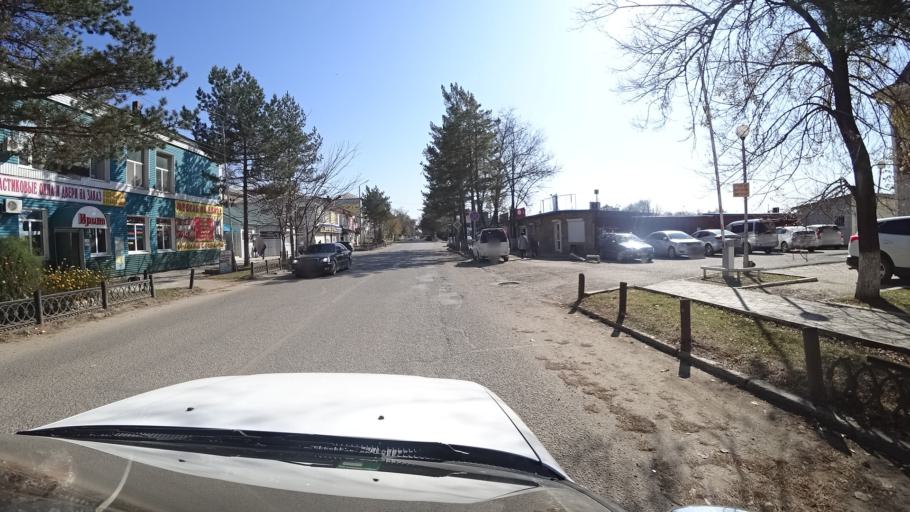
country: RU
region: Primorskiy
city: Dal'nerechensk
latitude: 45.9307
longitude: 133.7313
